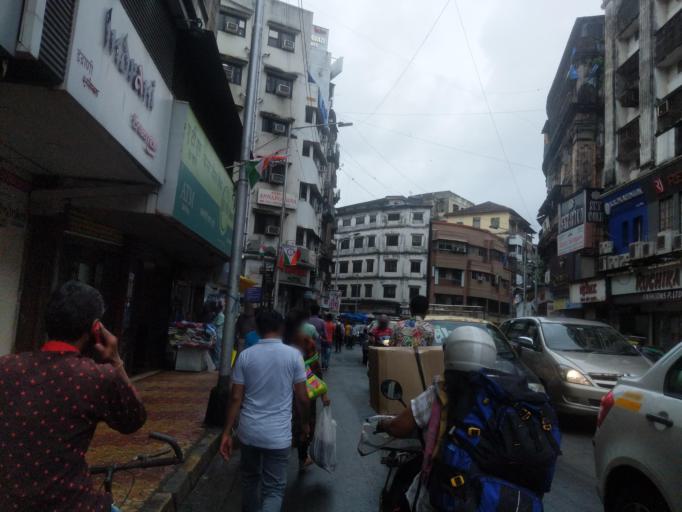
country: IN
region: Maharashtra
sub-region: Raigarh
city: Uran
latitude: 18.9504
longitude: 72.8288
